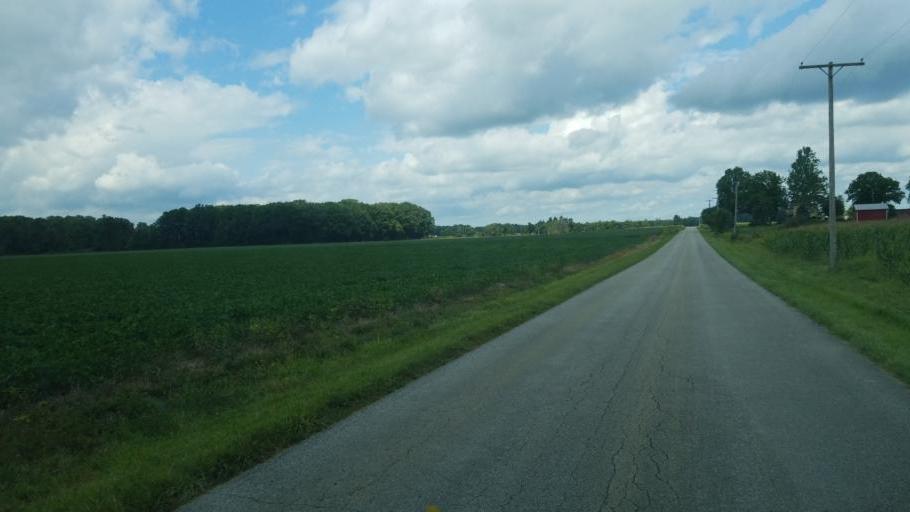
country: US
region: Ohio
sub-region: Huron County
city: Monroeville
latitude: 41.1611
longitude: -82.7568
